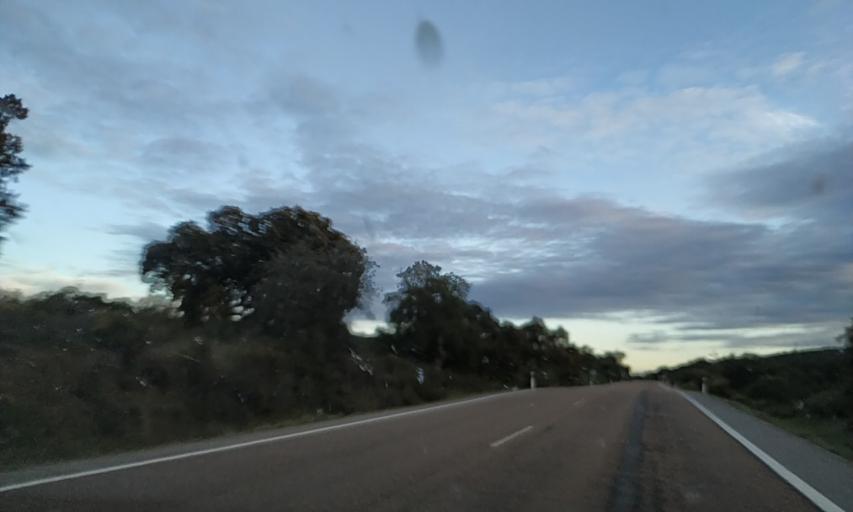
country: ES
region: Extremadura
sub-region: Provincia de Badajoz
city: Puebla de Obando
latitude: 39.2856
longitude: -6.5221
